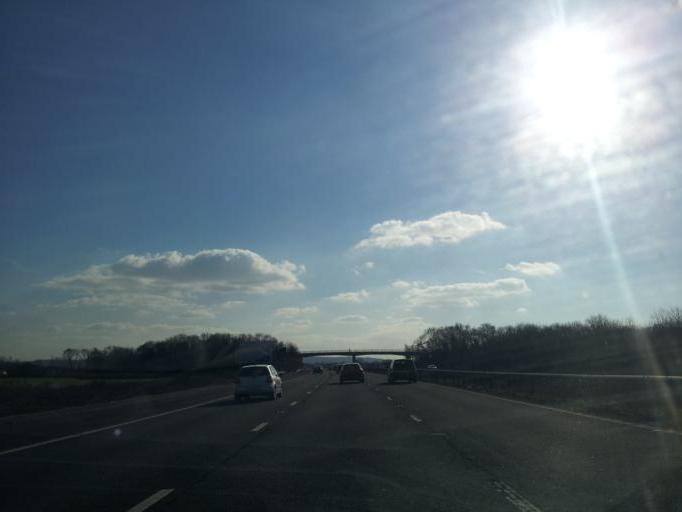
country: GB
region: England
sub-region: North Somerset
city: St. Georges
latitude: 51.3766
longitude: -2.8829
